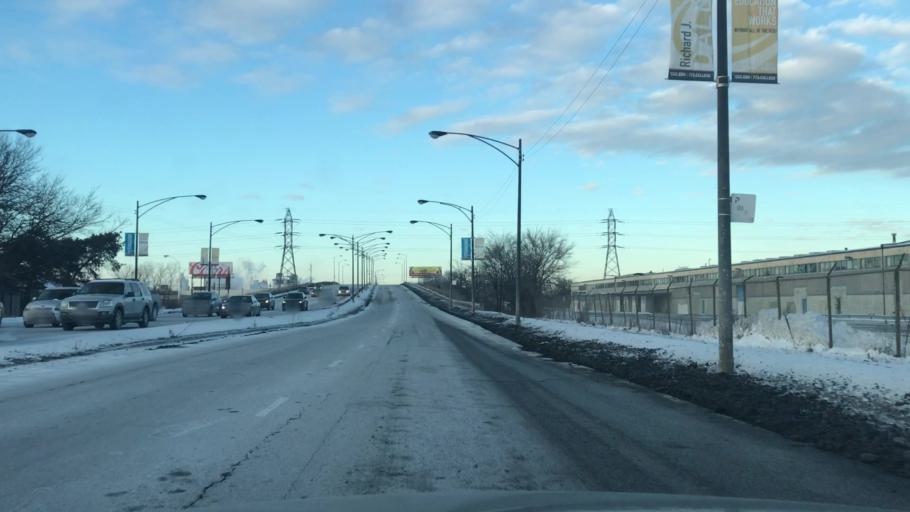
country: US
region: Illinois
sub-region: Cook County
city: Hometown
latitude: 41.7584
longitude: -87.7221
